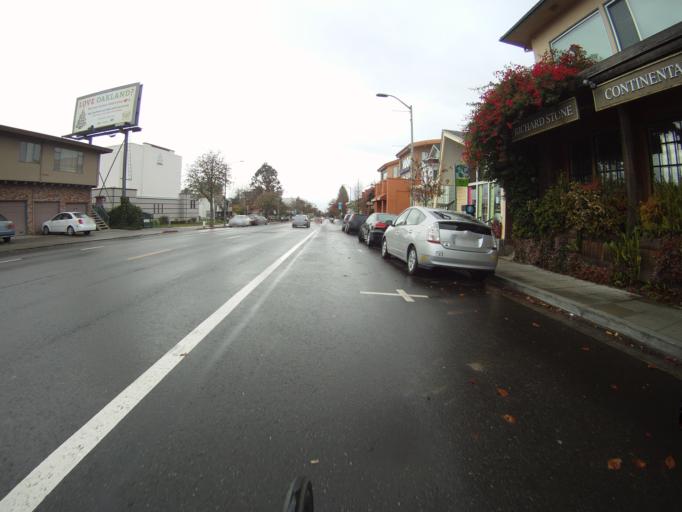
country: US
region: California
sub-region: Alameda County
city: Piedmont
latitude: 37.8293
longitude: -122.2487
